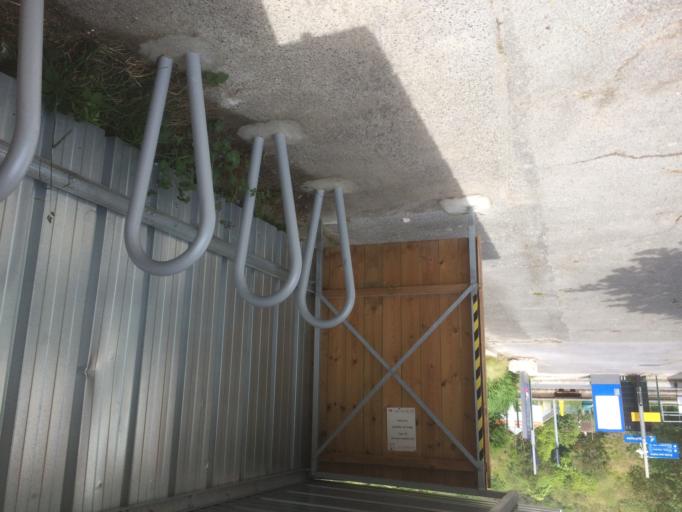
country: FR
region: Ile-de-France
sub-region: Departement des Yvelines
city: Jouy-en-Josas
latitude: 48.7590
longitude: 2.1920
